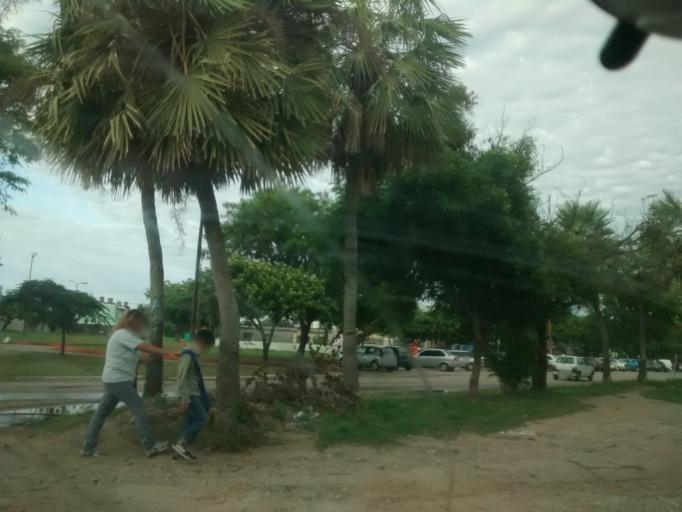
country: AR
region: Chaco
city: Fontana
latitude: -27.4473
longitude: -59.0142
